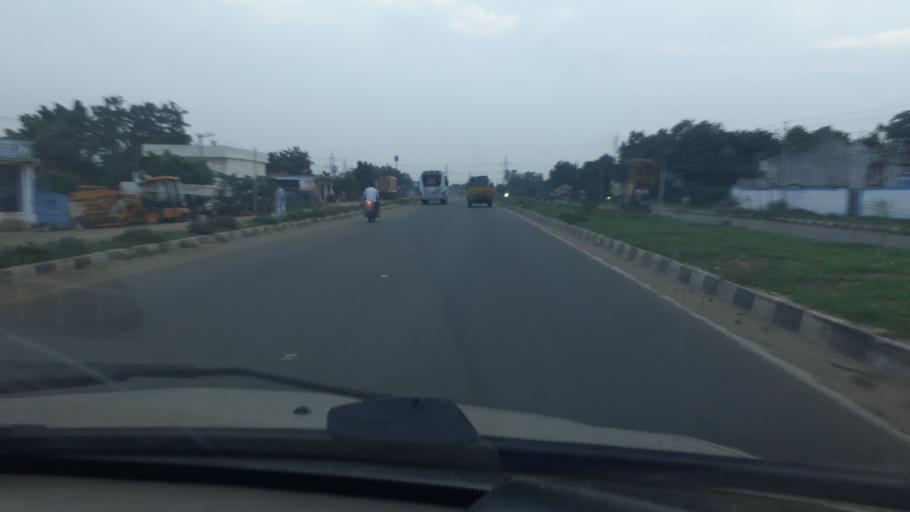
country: IN
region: Tamil Nadu
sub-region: Thoothukkudi
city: Korampallam
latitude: 8.7767
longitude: 78.0902
